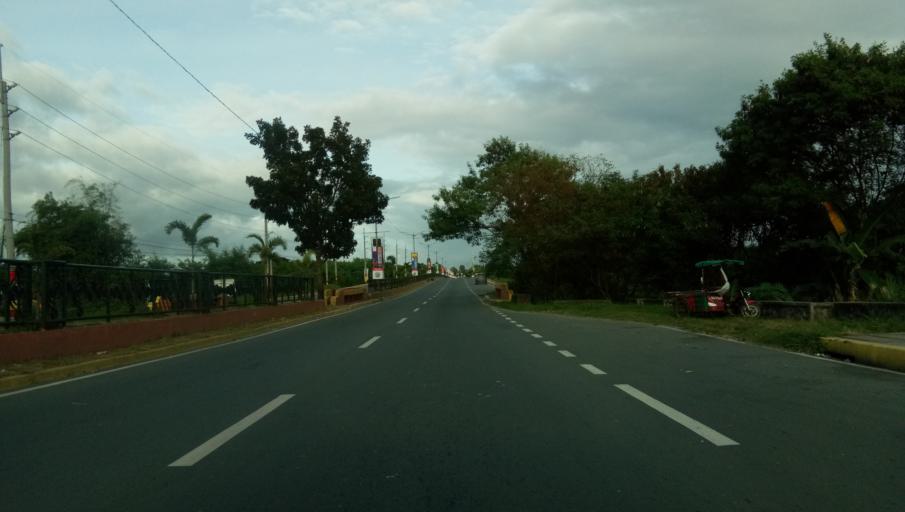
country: PH
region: Calabarzon
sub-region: Province of Cavite
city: Dasmarinas
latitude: 14.3755
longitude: 120.9466
